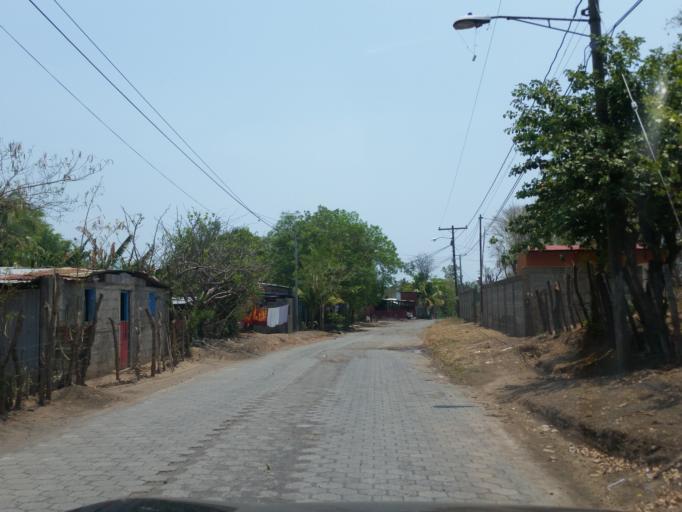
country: NI
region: Granada
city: Granada
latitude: 11.9298
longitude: -85.9700
